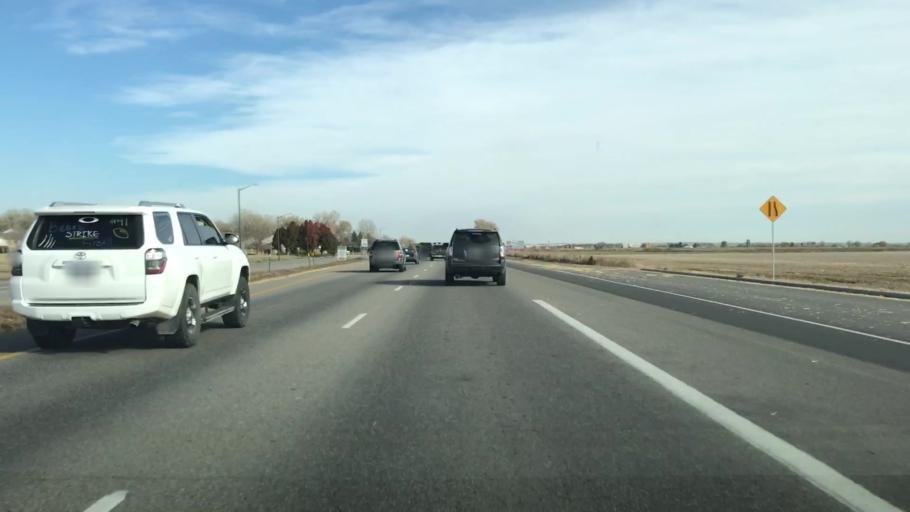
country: US
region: Colorado
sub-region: Larimer County
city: Loveland
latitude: 40.4072
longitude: -105.0196
